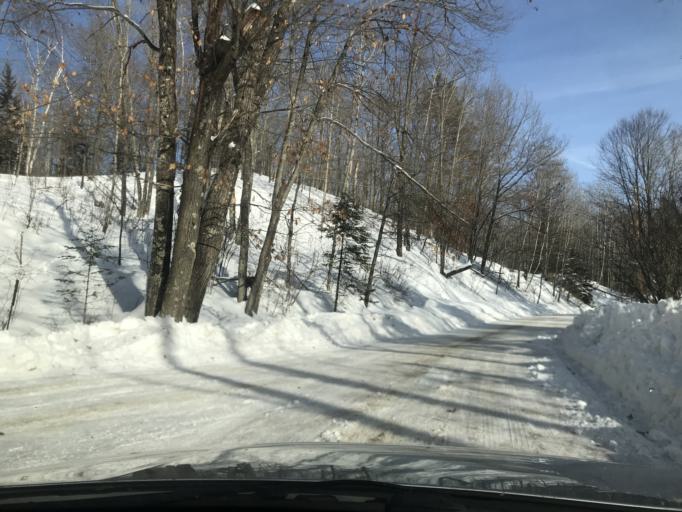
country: US
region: Wisconsin
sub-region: Menominee County
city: Legend Lake
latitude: 45.3439
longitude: -88.4571
